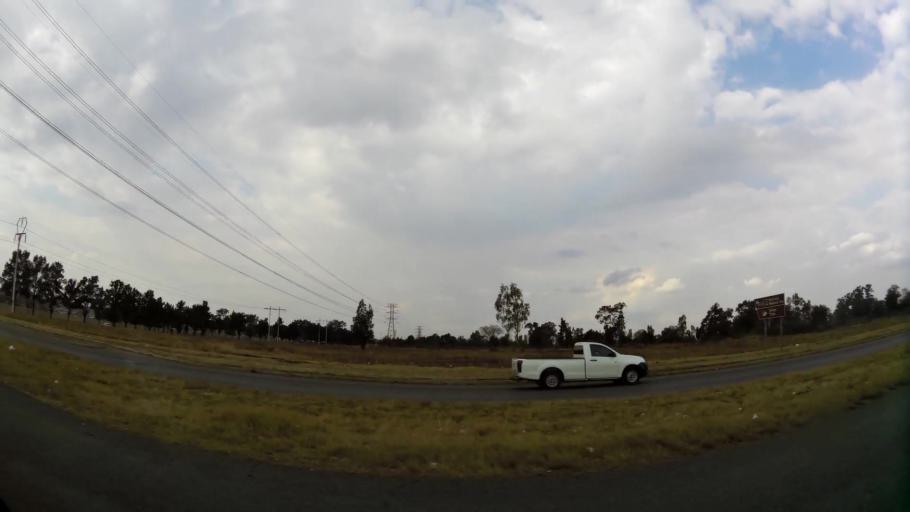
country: ZA
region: Gauteng
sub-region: Sedibeng District Municipality
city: Vanderbijlpark
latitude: -26.6721
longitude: 27.8374
